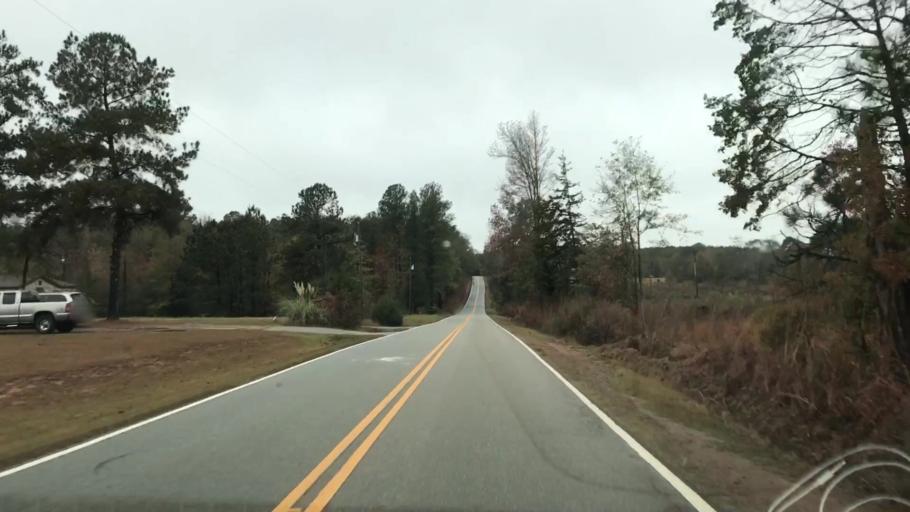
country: US
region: South Carolina
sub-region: Greenwood County
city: Ninety Six
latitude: 34.3080
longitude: -81.9723
